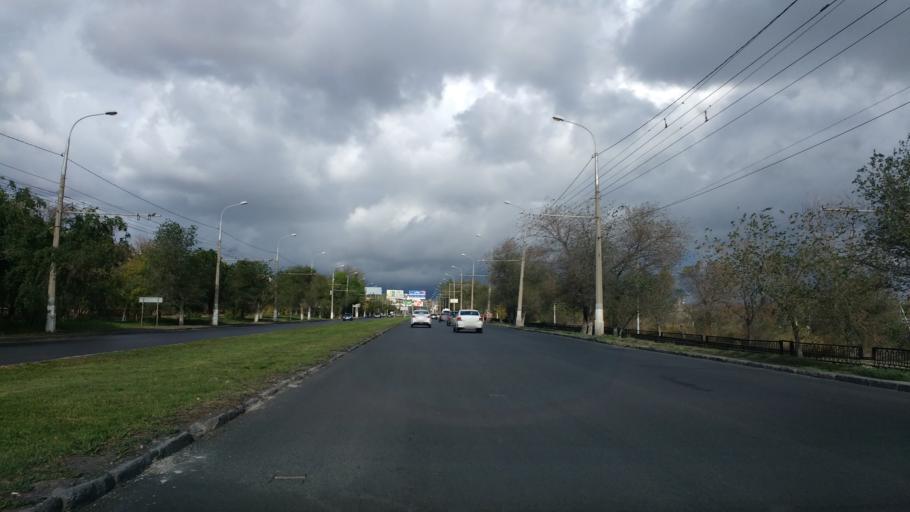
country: RU
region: Volgograd
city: Krasnoslobodsk
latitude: 48.7666
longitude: 44.5630
